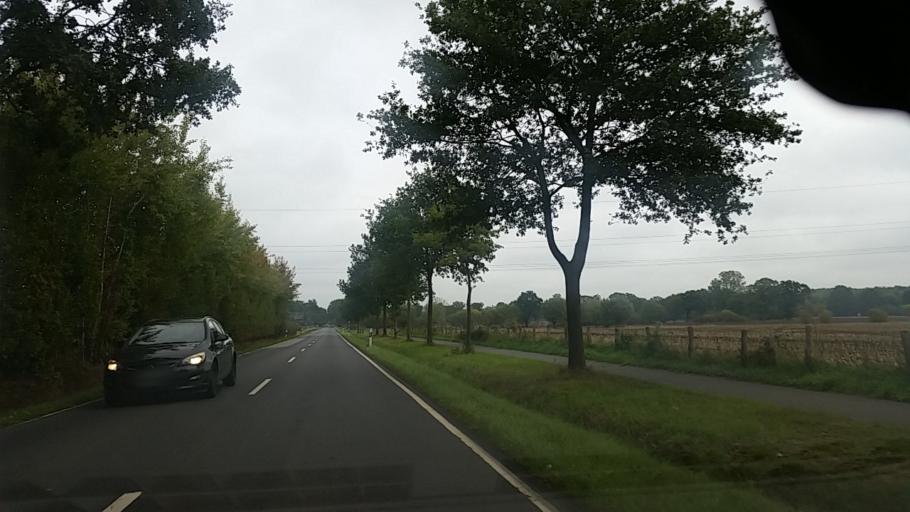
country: DE
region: Schleswig-Holstein
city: Kaltenkirchen
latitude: 53.8544
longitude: 9.9696
